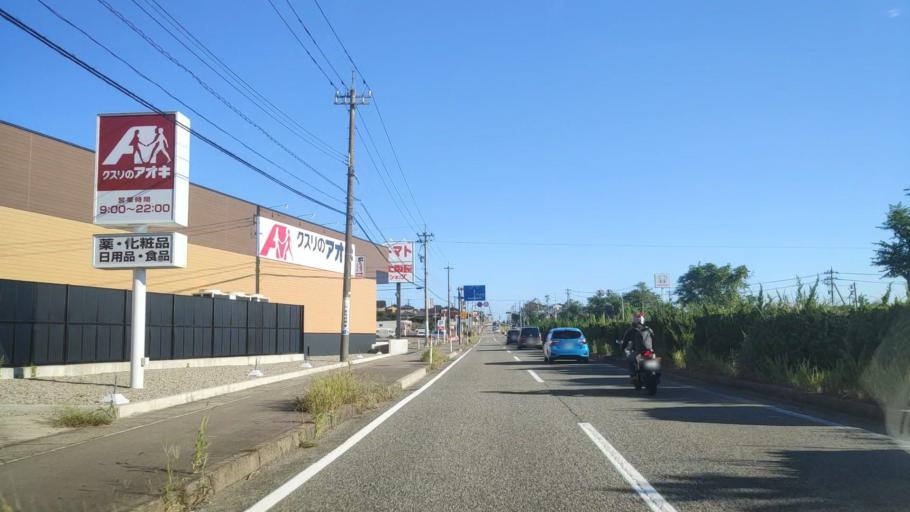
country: JP
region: Ishikawa
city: Tsubata
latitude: 36.7211
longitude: 136.6982
